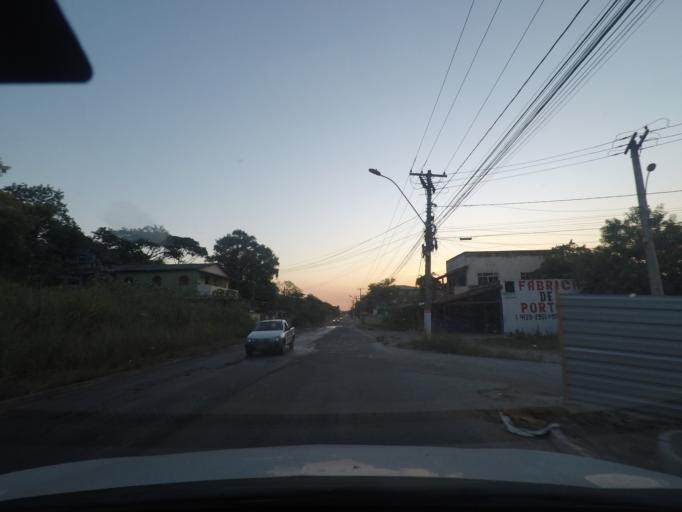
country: BR
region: Rio de Janeiro
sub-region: Niteroi
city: Niteroi
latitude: -22.9510
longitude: -42.9724
